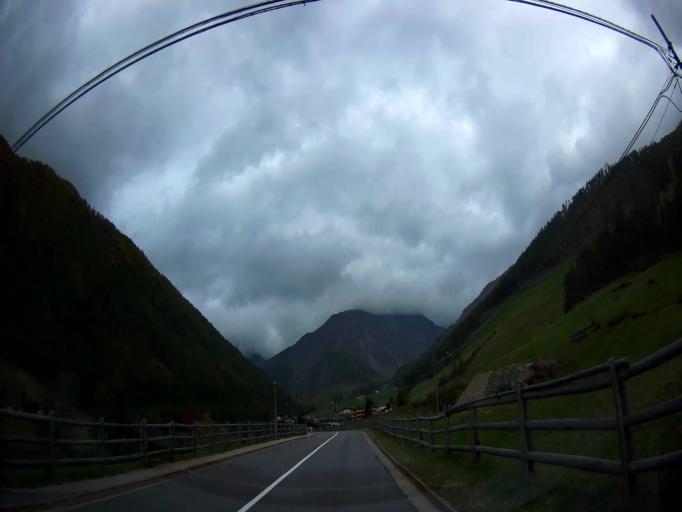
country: IT
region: Trentino-Alto Adige
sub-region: Bolzano
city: Senales
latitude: 46.7231
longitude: 10.8605
